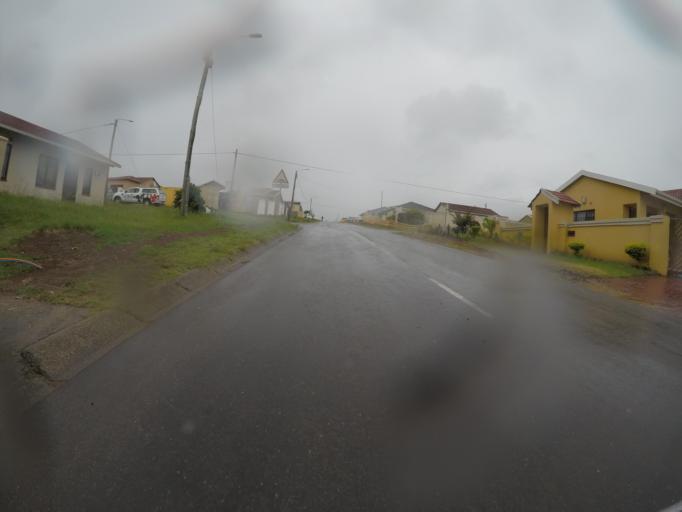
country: ZA
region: Eastern Cape
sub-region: Buffalo City Metropolitan Municipality
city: East London
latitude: -32.9971
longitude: 27.8420
